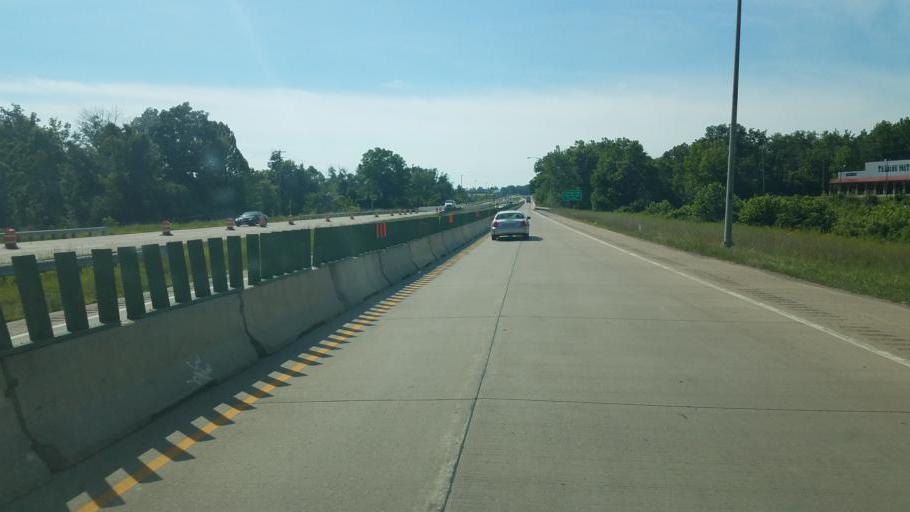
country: US
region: Ohio
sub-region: Athens County
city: The Plains
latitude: 39.3627
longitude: -82.1094
